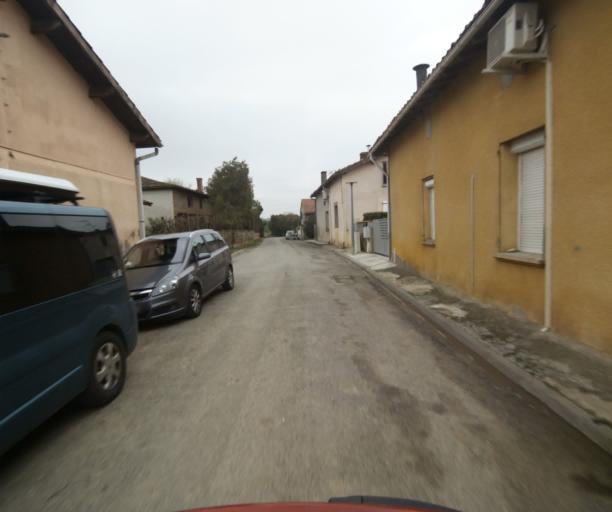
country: FR
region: Midi-Pyrenees
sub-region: Departement du Tarn-et-Garonne
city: Verdun-sur-Garonne
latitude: 43.8587
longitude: 1.2544
